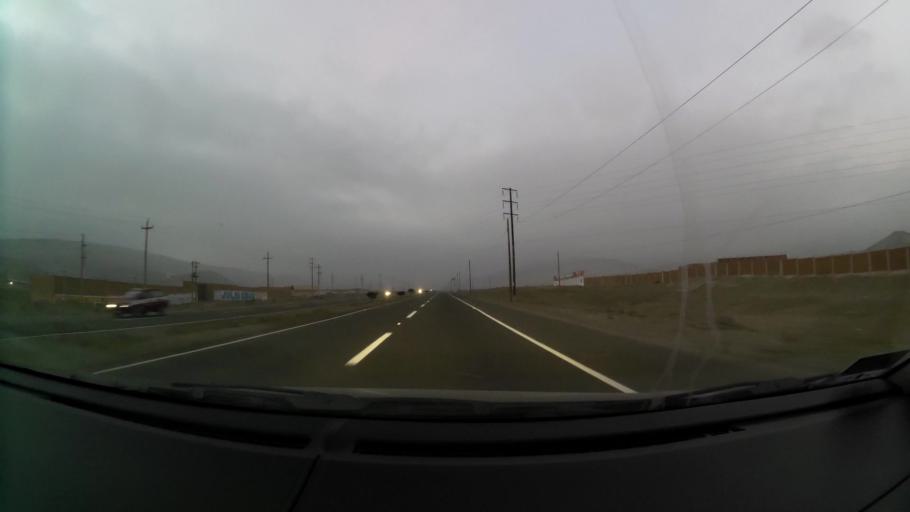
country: PE
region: Lima
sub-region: Lima
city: Santa Rosa
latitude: -11.7571
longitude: -77.1521
